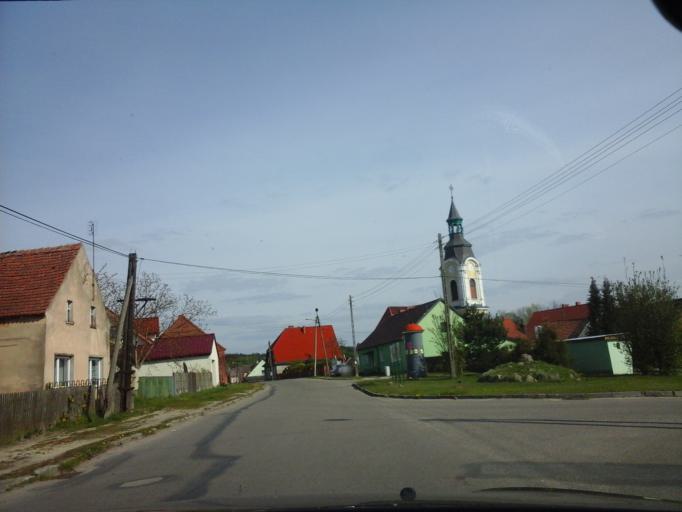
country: PL
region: West Pomeranian Voivodeship
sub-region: Powiat choszczenski
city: Krzecin
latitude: 53.0403
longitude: 15.5366
